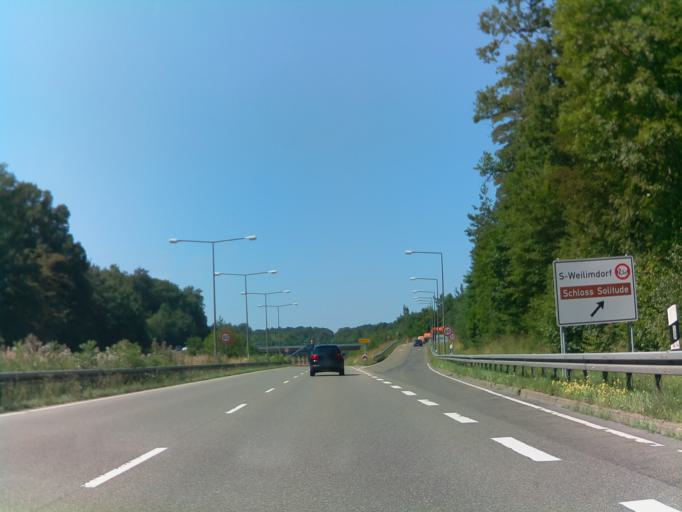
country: DE
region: Baden-Wuerttemberg
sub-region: Regierungsbezirk Stuttgart
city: Gerlingen
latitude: 48.7764
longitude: 9.0940
